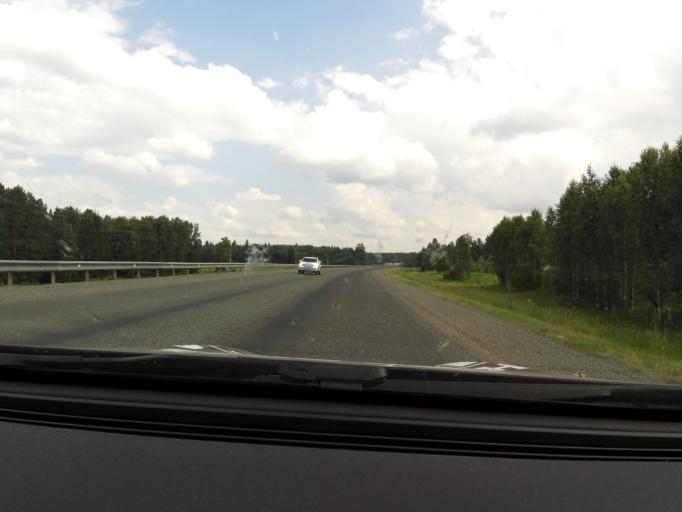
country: RU
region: Sverdlovsk
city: Ufimskiy
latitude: 56.7854
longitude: 58.3911
